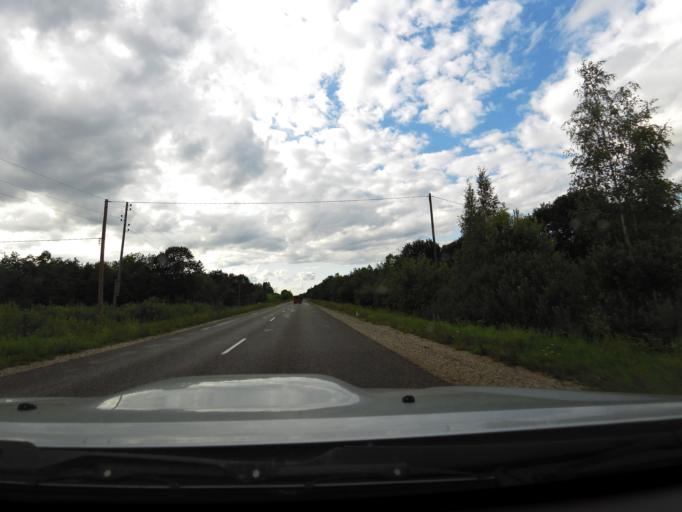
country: LV
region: Akniste
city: Akniste
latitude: 55.9943
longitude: 25.9708
